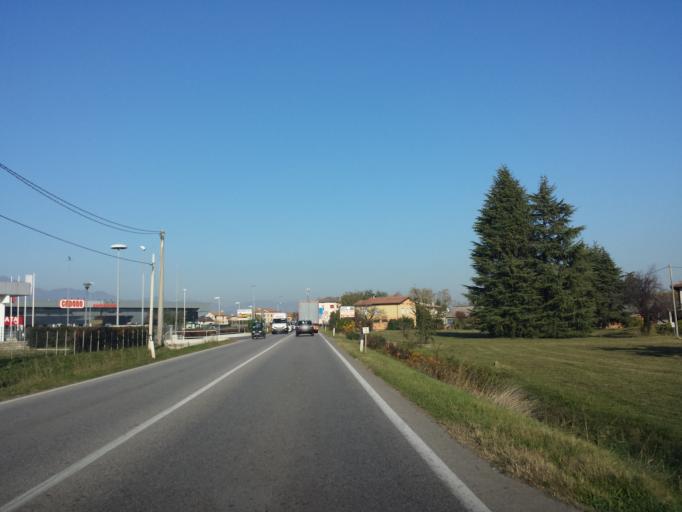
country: IT
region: Veneto
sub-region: Provincia di Treviso
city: Cornuda
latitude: 45.8111
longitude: 12.0109
